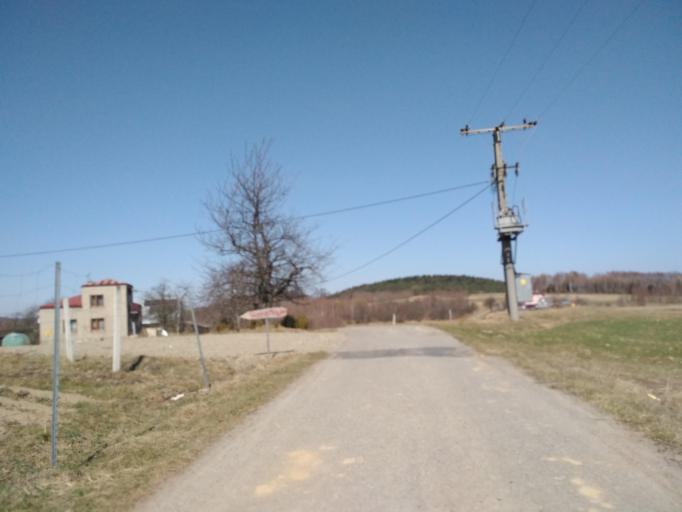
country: PL
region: Subcarpathian Voivodeship
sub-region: Powiat brzozowski
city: Jablonica Polska
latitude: 49.7392
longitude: 21.8954
